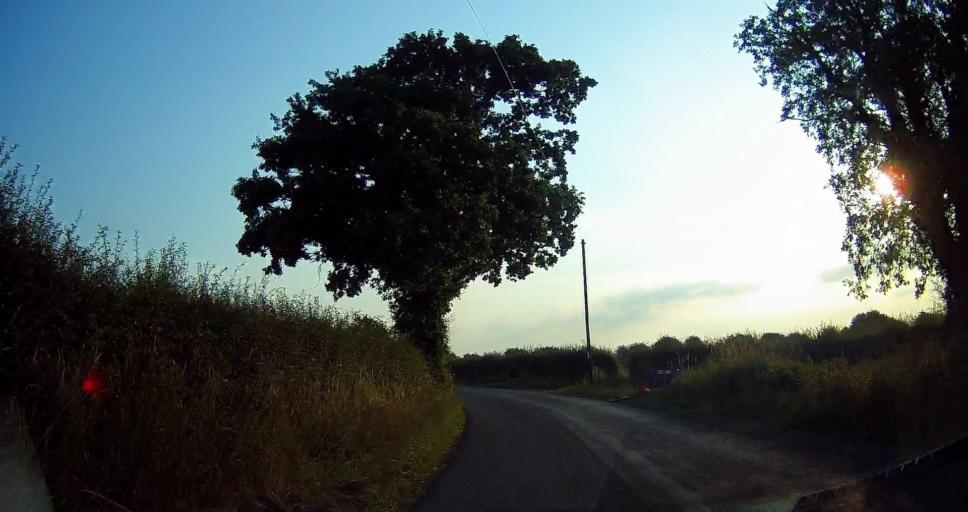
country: GB
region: England
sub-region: Cheshire East
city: Nantwich
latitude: 53.0077
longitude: -2.5272
